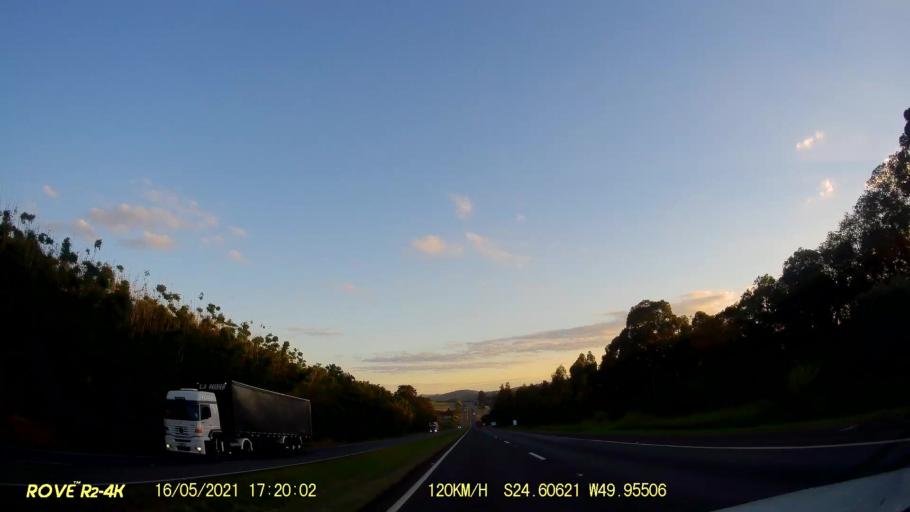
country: BR
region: Parana
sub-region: Pirai Do Sul
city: Pirai do Sul
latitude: -24.6065
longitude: -49.9553
